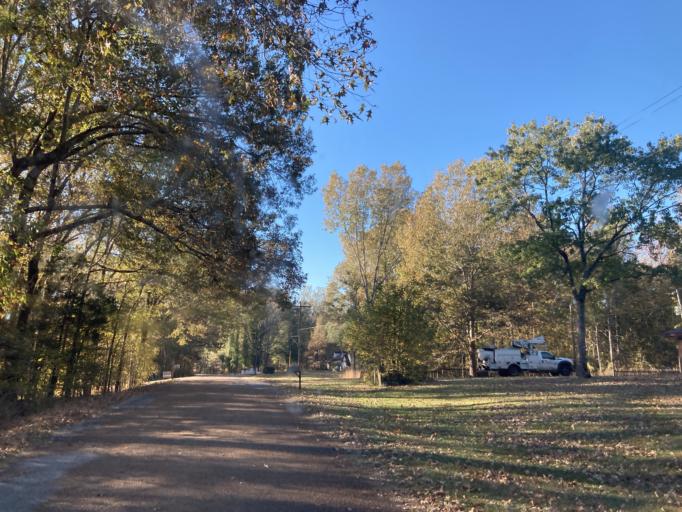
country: US
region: Mississippi
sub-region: Yazoo County
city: Yazoo City
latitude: 32.7964
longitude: -90.3555
